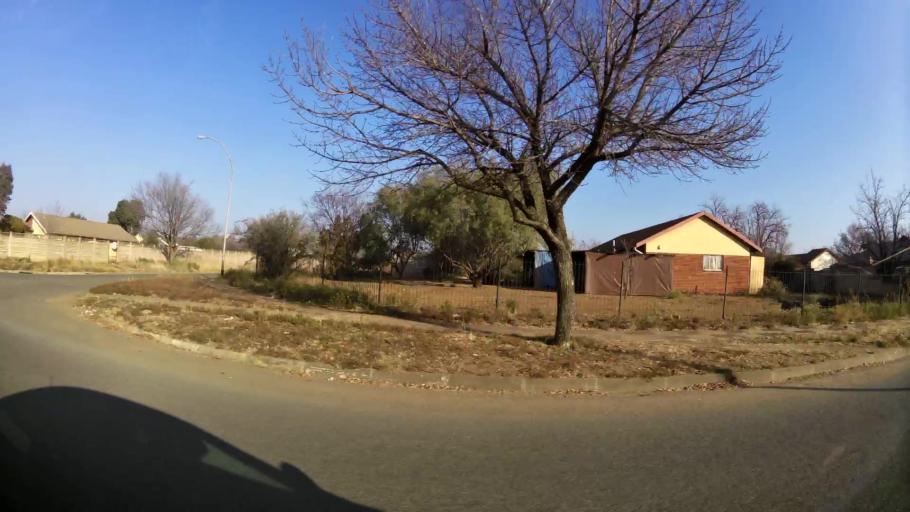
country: ZA
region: Orange Free State
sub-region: Mangaung Metropolitan Municipality
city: Bloemfontein
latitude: -29.1490
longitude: 26.2136
